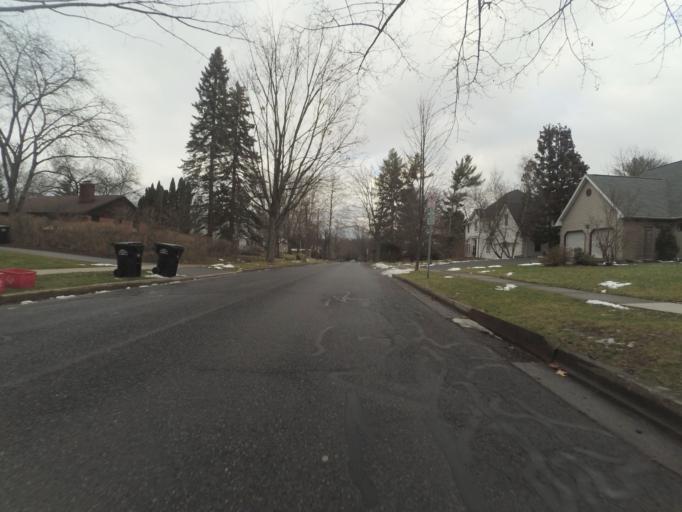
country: US
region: Pennsylvania
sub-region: Centre County
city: State College
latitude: 40.7962
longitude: -77.8476
